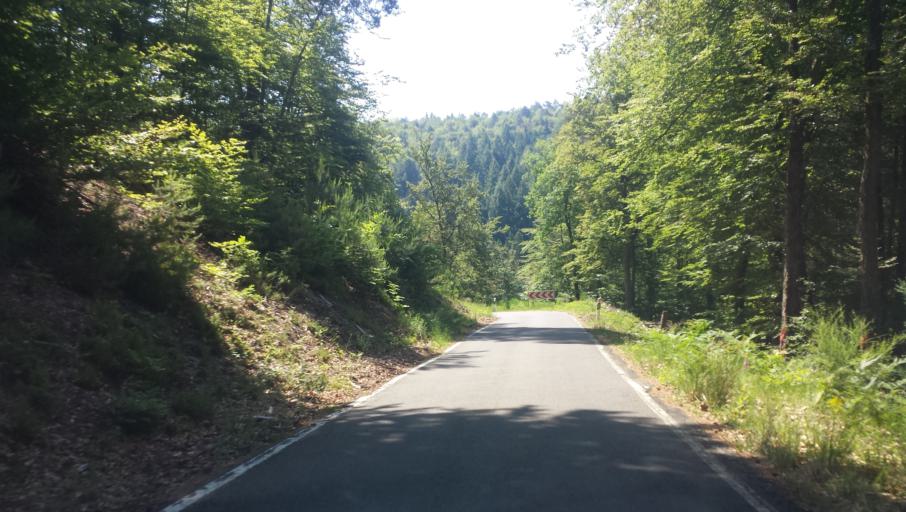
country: DE
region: Rheinland-Pfalz
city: Elmstein
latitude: 49.3599
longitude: 7.9194
